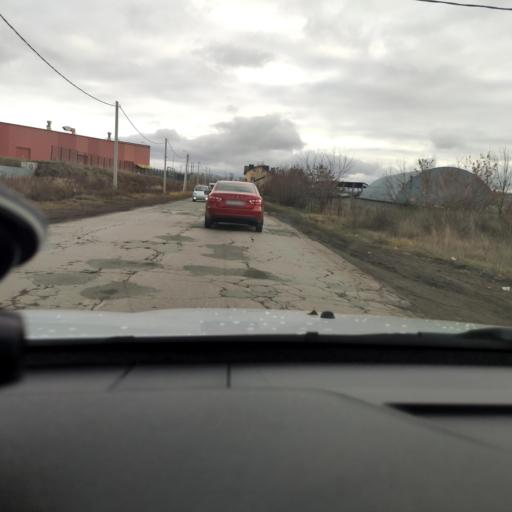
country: RU
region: Samara
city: Petra-Dubrava
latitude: 53.3023
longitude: 50.3584
